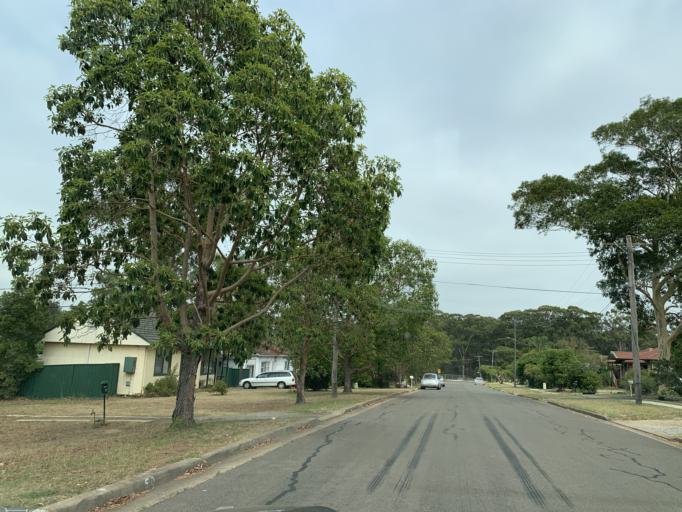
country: AU
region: New South Wales
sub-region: Blacktown
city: Doonside
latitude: -33.7626
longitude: 150.8876
